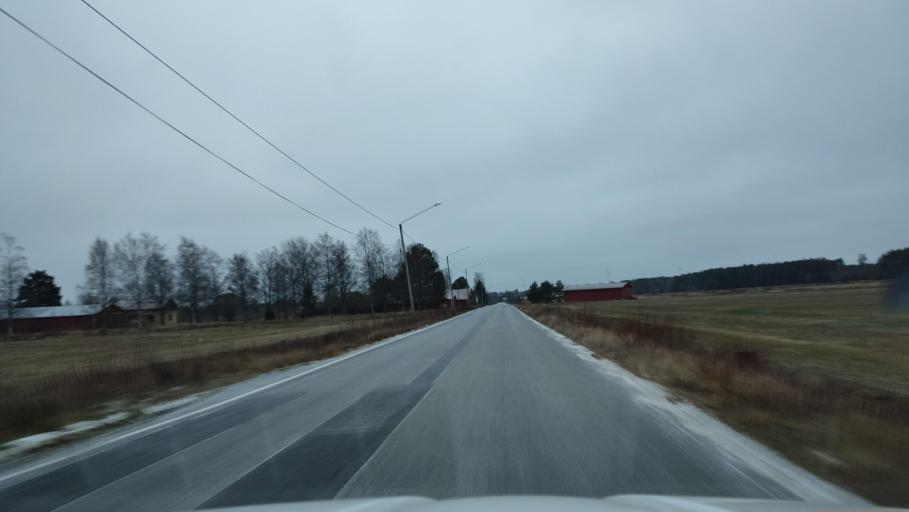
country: FI
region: Southern Ostrobothnia
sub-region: Suupohja
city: Karijoki
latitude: 62.2403
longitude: 21.6615
